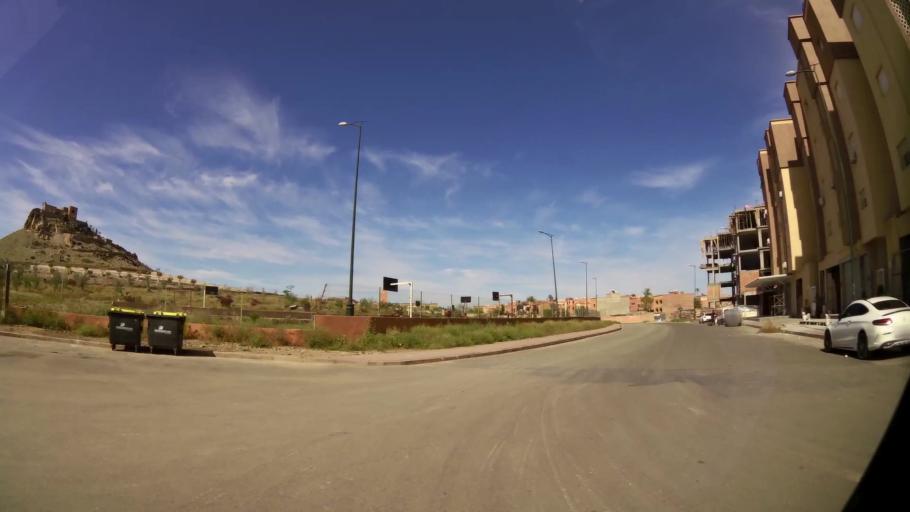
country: MA
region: Marrakech-Tensift-Al Haouz
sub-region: Marrakech
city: Marrakesh
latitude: 31.6606
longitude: -8.0212
